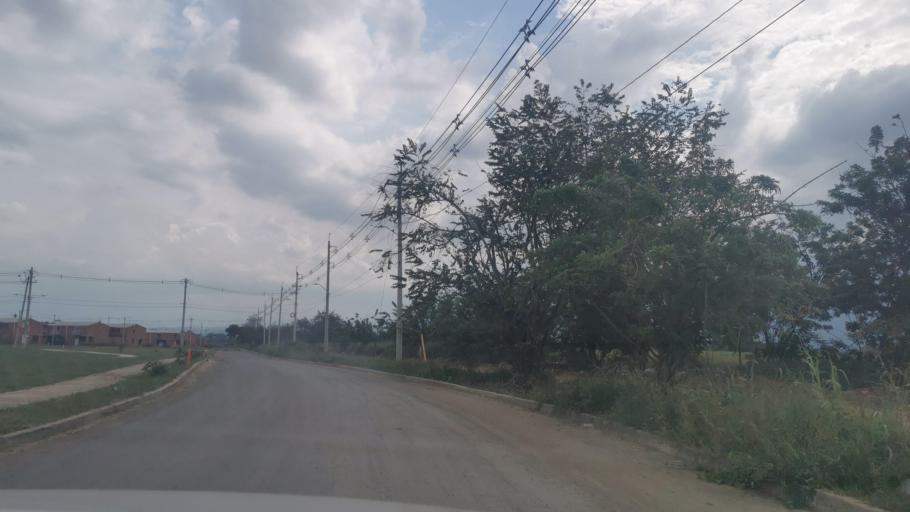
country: CO
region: Valle del Cauca
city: Jamundi
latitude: 3.2374
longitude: -76.5257
